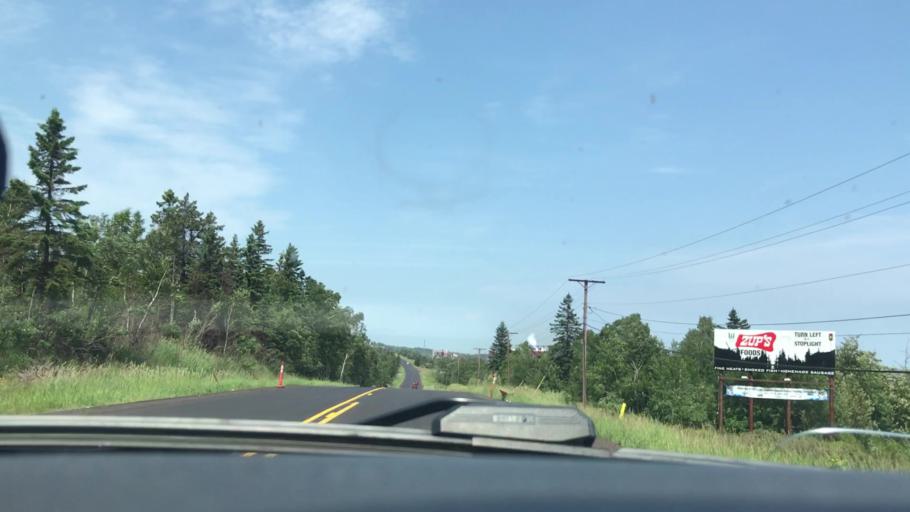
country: US
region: Minnesota
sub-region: Lake County
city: Silver Bay
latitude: 47.2740
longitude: -91.2762
